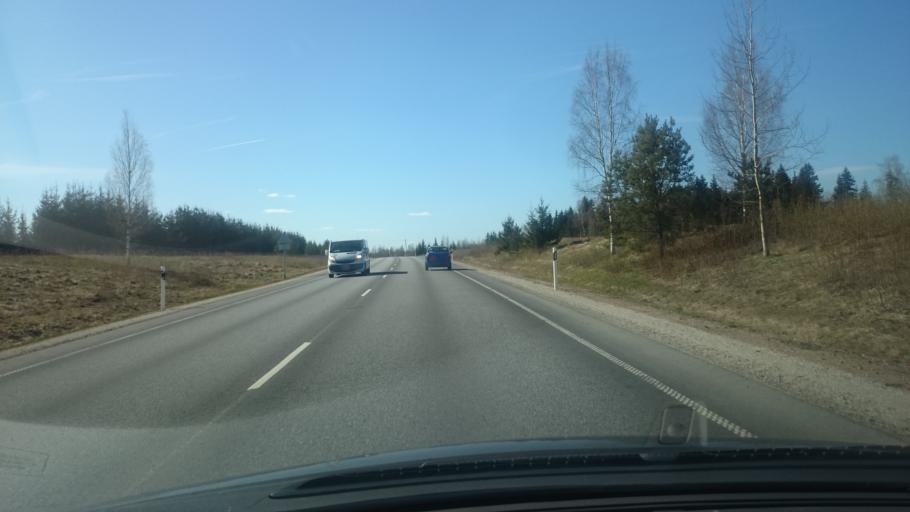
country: EE
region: Tartu
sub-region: UElenurme vald
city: Ulenurme
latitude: 58.3486
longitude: 26.9354
